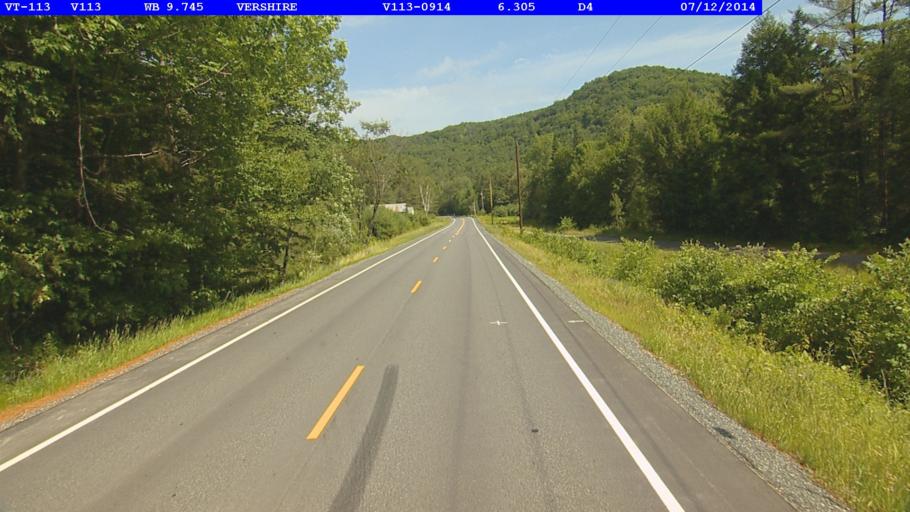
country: US
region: New Hampshire
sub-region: Grafton County
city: Orford
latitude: 43.9544
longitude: -72.2777
